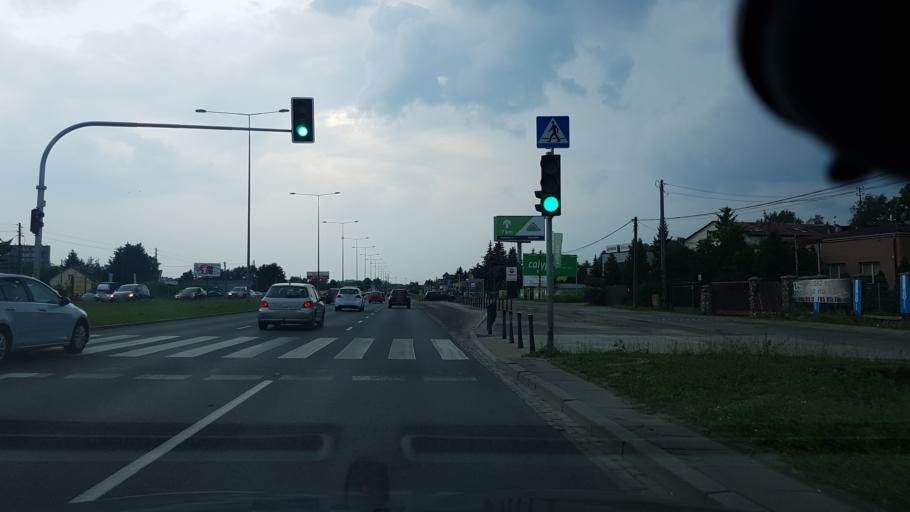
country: PL
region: Masovian Voivodeship
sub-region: Warszawa
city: Bialoleka
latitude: 52.3380
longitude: 20.9583
